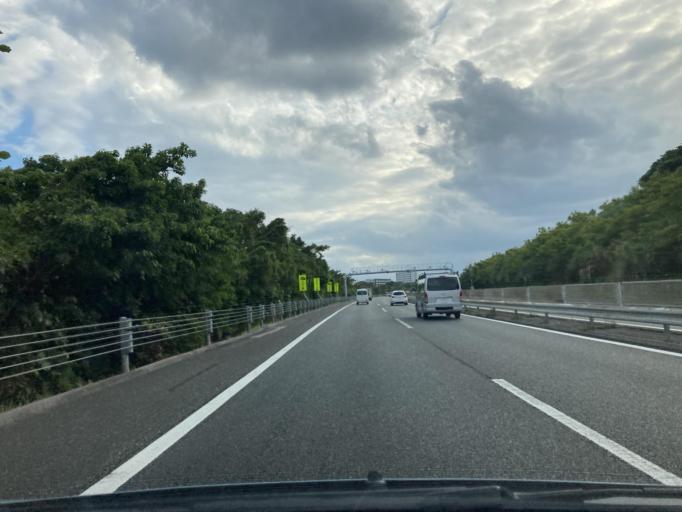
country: JP
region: Okinawa
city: Ginowan
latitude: 26.2639
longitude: 127.7732
